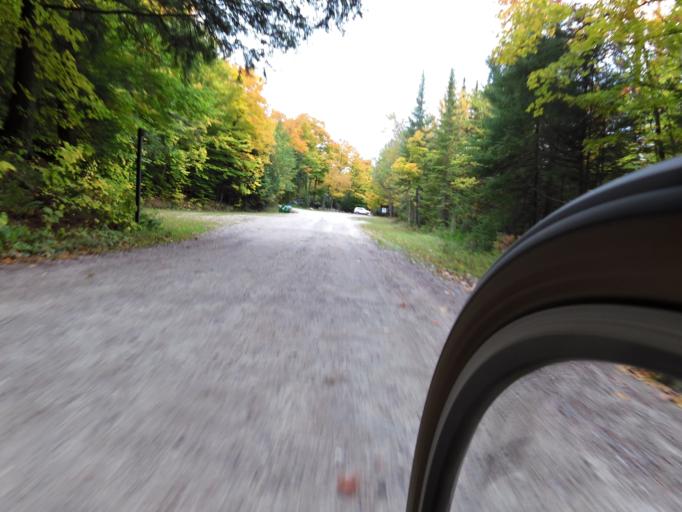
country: CA
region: Quebec
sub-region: Outaouais
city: Wakefield
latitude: 45.6017
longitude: -76.0414
